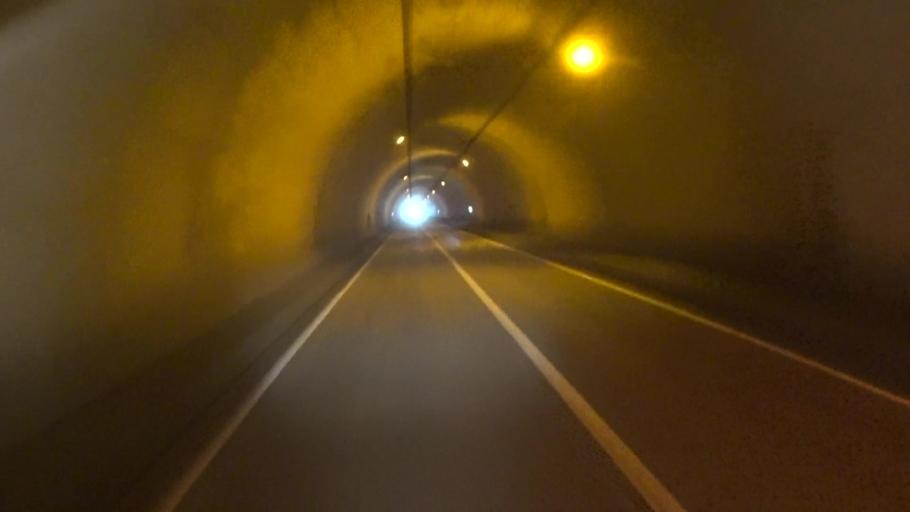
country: JP
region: Kyoto
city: Maizuru
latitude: 35.5142
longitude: 135.3771
